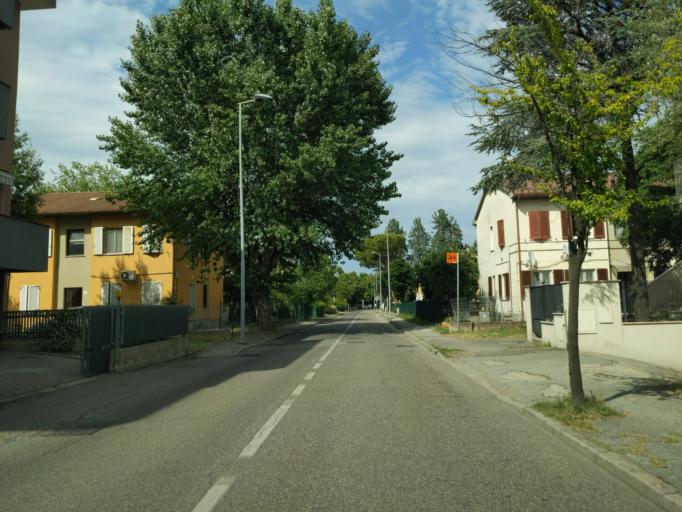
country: IT
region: Emilia-Romagna
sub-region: Provincia di Rimini
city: Rimini
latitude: 44.0447
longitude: 12.5795
